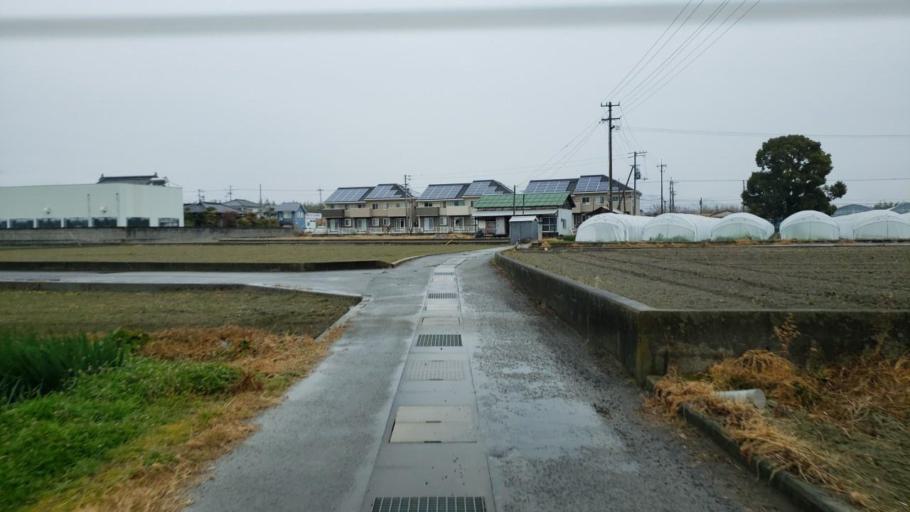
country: JP
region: Tokushima
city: Kamojimacho-jogejima
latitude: 34.0613
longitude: 134.2840
